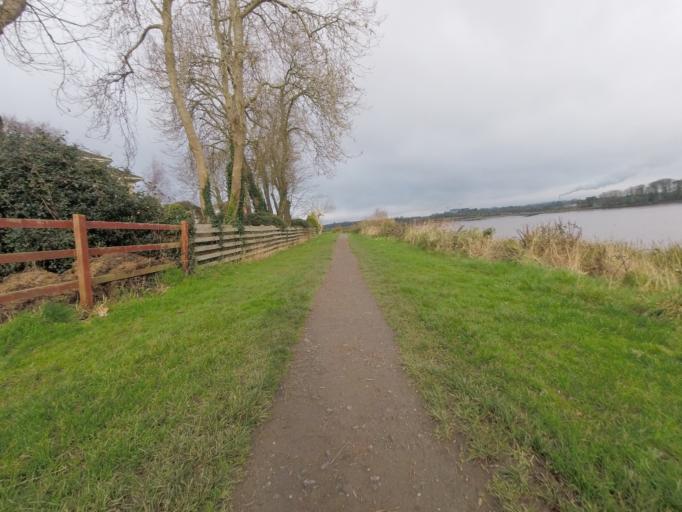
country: IE
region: Munster
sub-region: Waterford
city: Waterford
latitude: 52.2517
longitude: -7.0678
